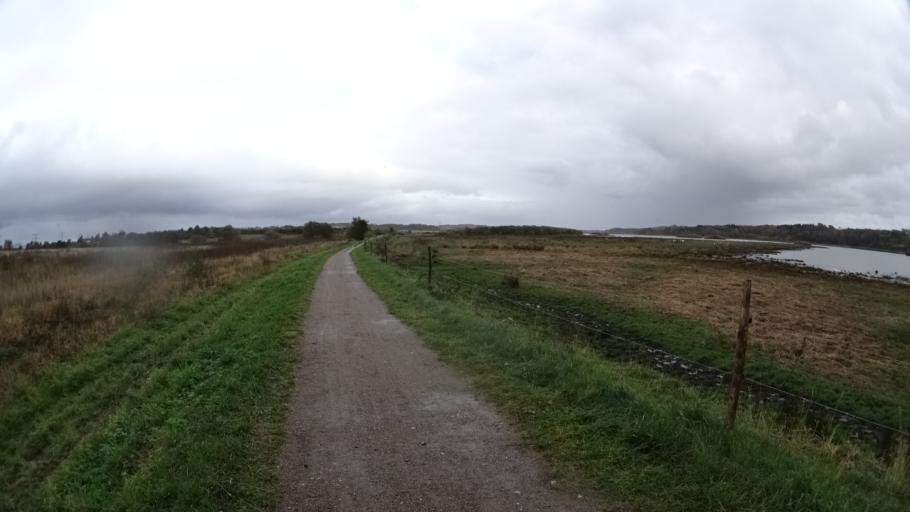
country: DK
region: Central Jutland
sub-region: Arhus Kommune
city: Kolt
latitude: 56.1400
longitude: 10.0542
